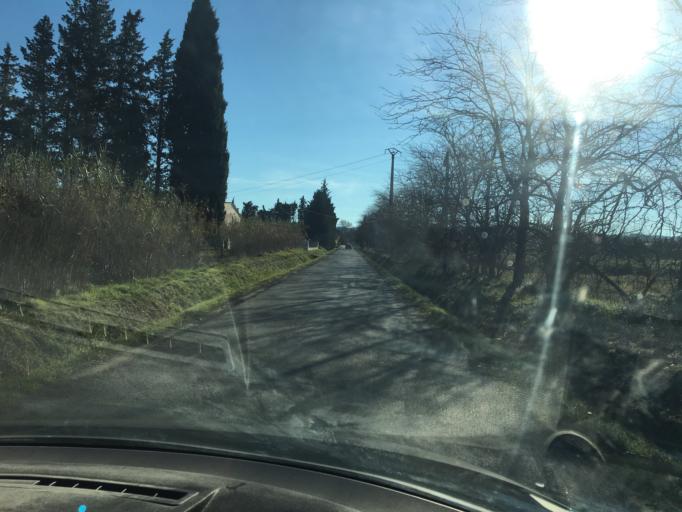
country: FR
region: Provence-Alpes-Cote d'Azur
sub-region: Departement des Bouches-du-Rhone
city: Maillane
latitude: 43.8006
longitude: 4.7885
